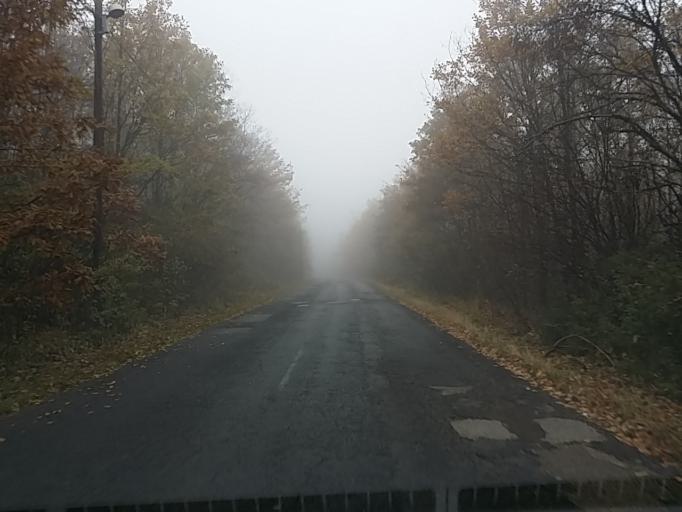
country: HU
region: Heves
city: Abasar
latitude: 47.8074
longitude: 19.9757
